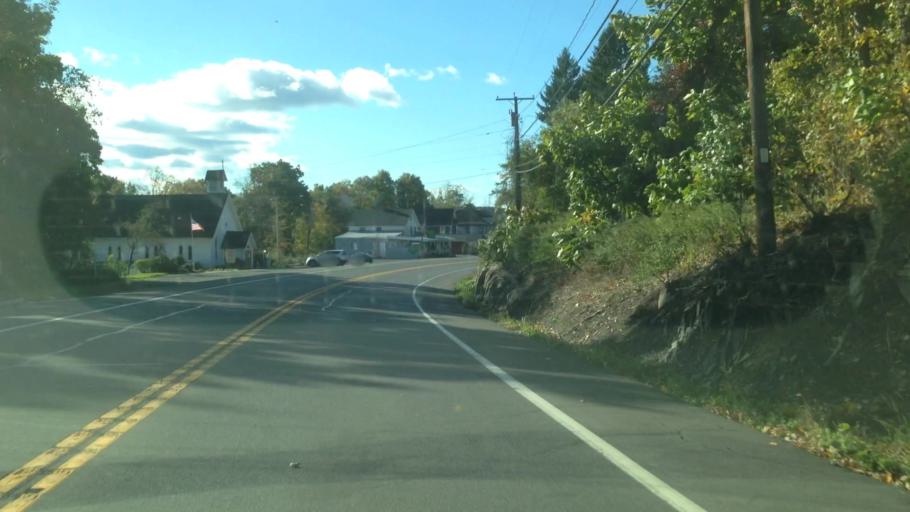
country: US
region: New York
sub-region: Dutchess County
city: Hyde Park
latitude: 41.8335
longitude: -73.9648
